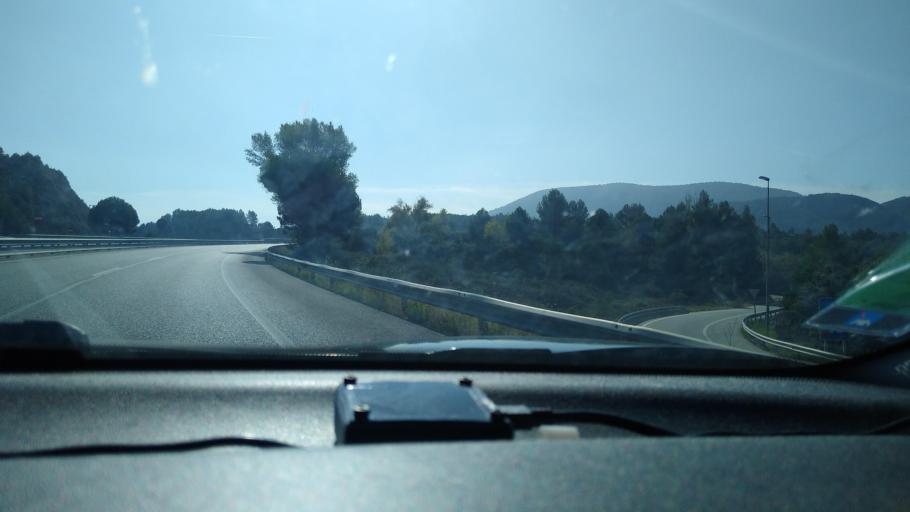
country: ES
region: Catalonia
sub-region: Provincia de Barcelona
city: Olesa de Montserrat
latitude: 41.5925
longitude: 1.9068
